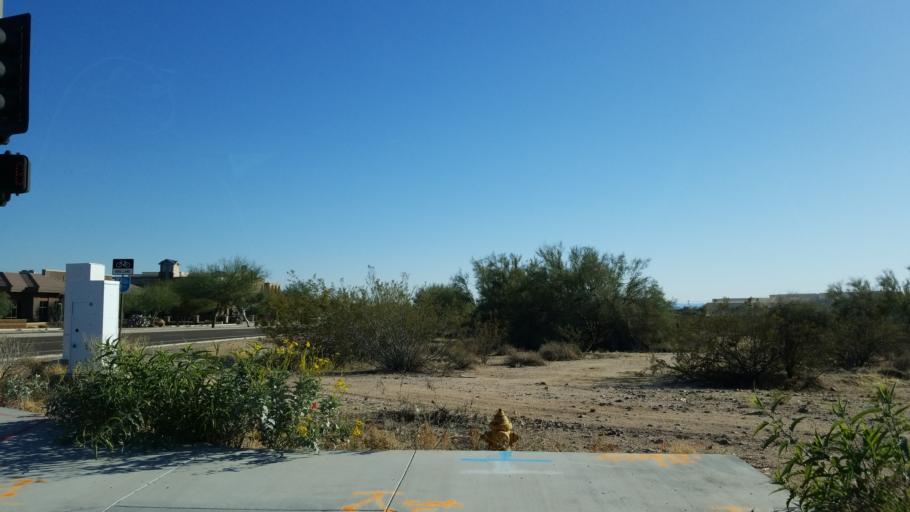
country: US
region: Arizona
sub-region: Maricopa County
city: Carefree
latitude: 33.6914
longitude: -111.9169
